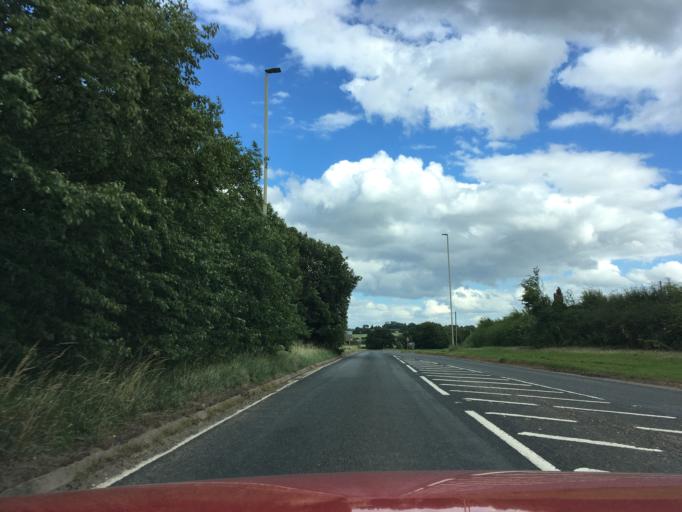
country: GB
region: England
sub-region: Warwickshire
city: Atherstone
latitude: 52.6274
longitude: -1.4858
